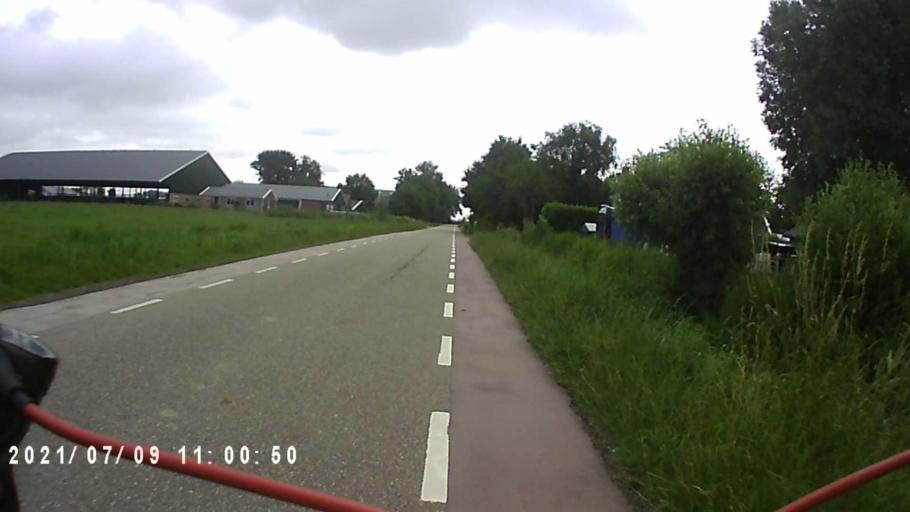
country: NL
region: Groningen
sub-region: Gemeente Bedum
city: Bedum
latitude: 53.2745
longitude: 6.7054
